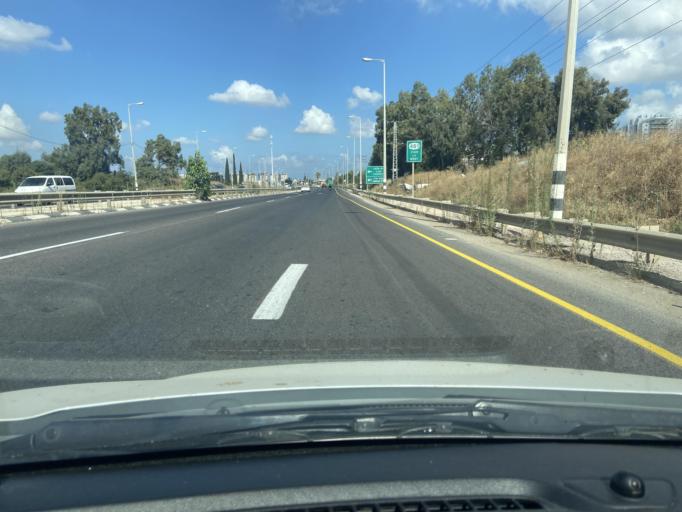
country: IL
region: Central District
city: Yehud
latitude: 32.0259
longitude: 34.8965
